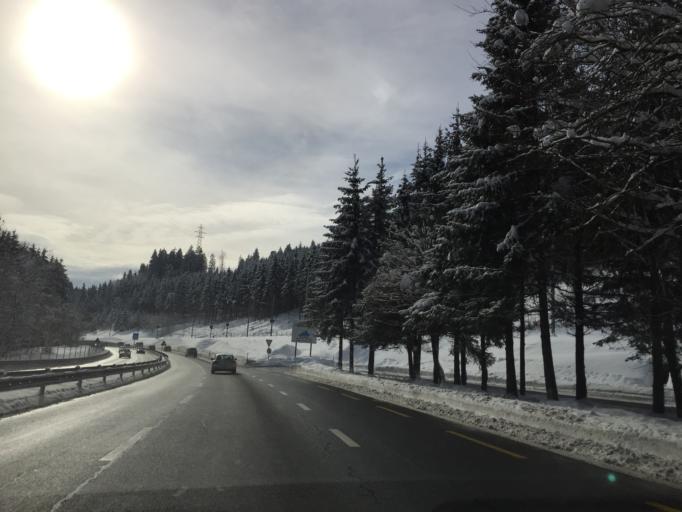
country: CH
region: Schwyz
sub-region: Bezirk Hoefe
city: Schindellegi
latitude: 47.1659
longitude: 8.7292
